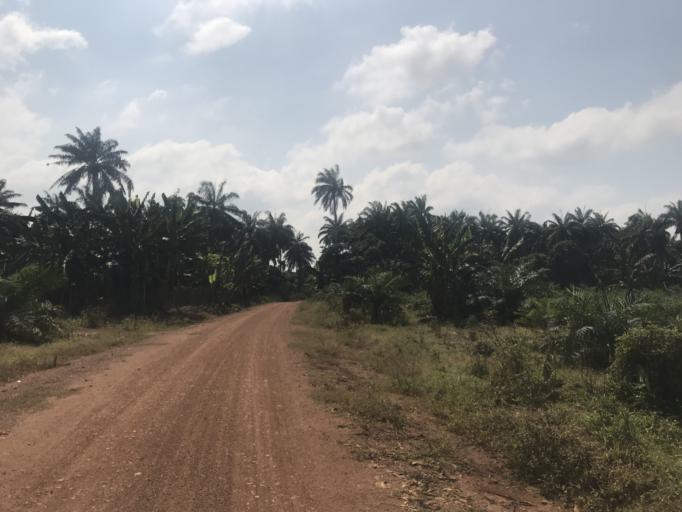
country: NG
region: Osun
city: Ibokun
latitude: 7.8189
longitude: 4.6444
